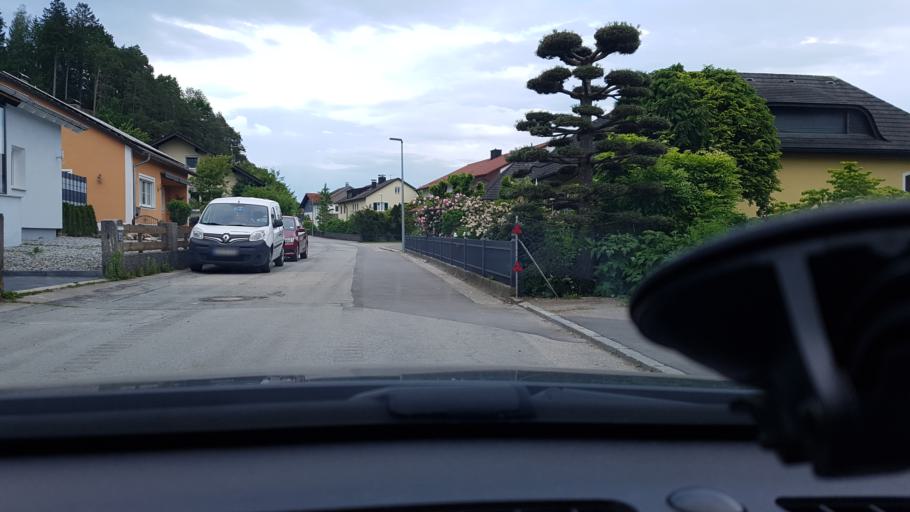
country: AT
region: Upper Austria
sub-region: Politischer Bezirk Braunau am Inn
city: Braunau am Inn
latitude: 48.2764
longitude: 13.0427
